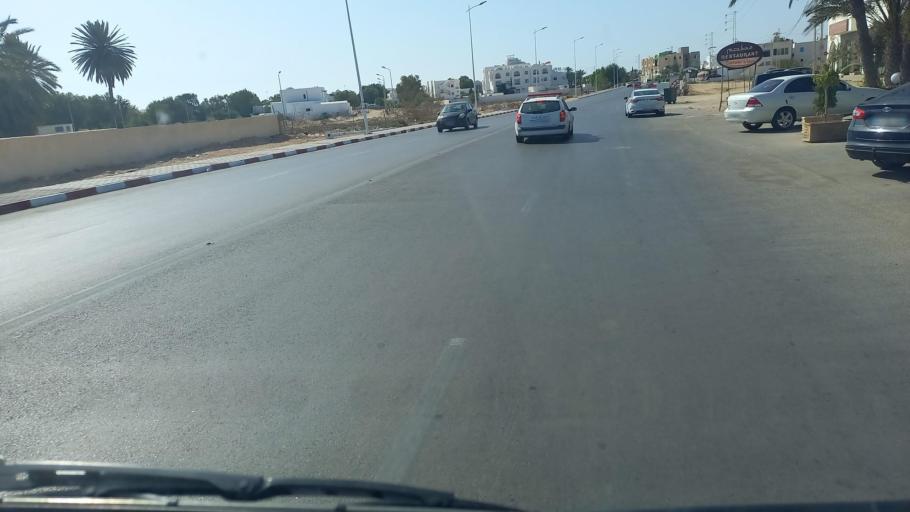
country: TN
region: Madanin
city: Midoun
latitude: 33.8465
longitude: 10.9876
